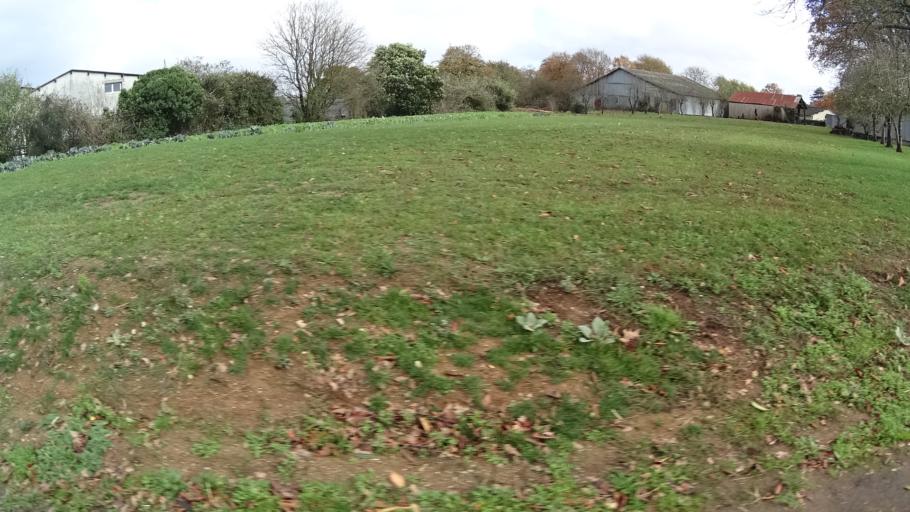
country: FR
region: Brittany
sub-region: Departement du Morbihan
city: Rieux
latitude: 47.5694
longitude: -2.1161
